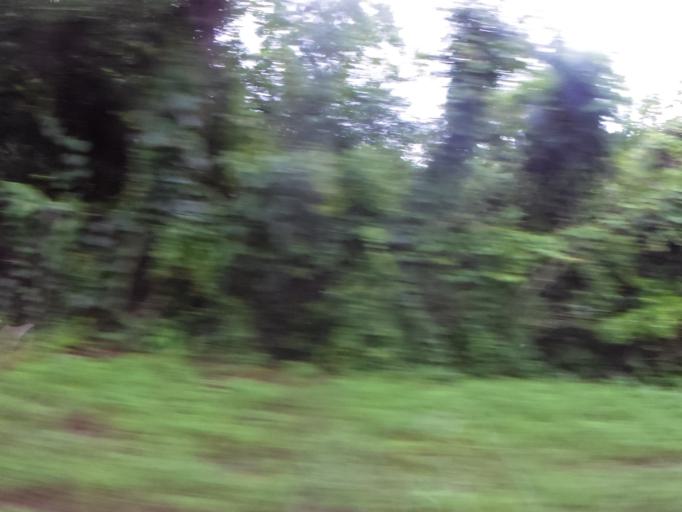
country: US
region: Florida
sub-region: Duval County
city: Jacksonville
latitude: 30.3557
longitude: -81.6327
